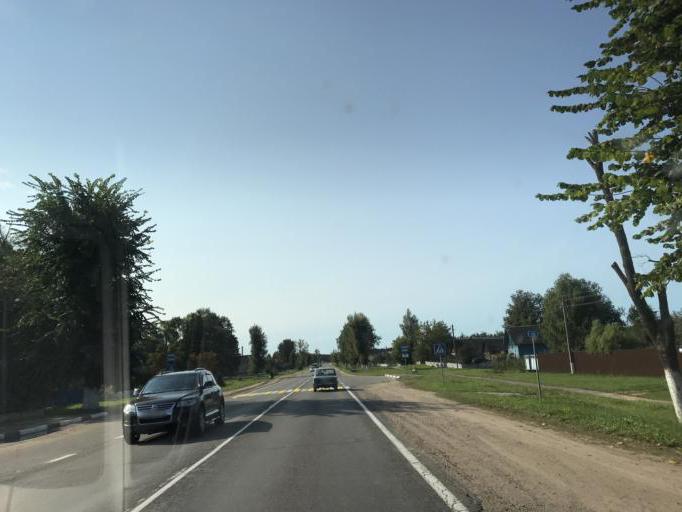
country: BY
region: Mogilev
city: Buynichy
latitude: 53.8310
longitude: 30.2440
